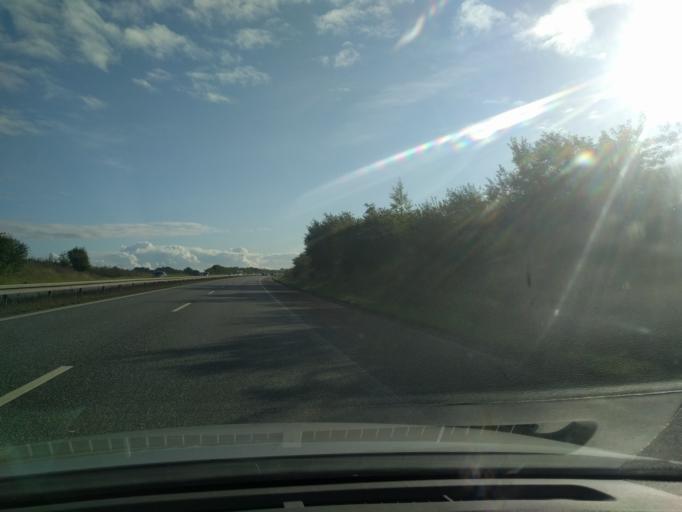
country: DK
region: Zealand
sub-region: Soro Kommune
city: Soro
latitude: 55.4505
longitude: 11.5768
